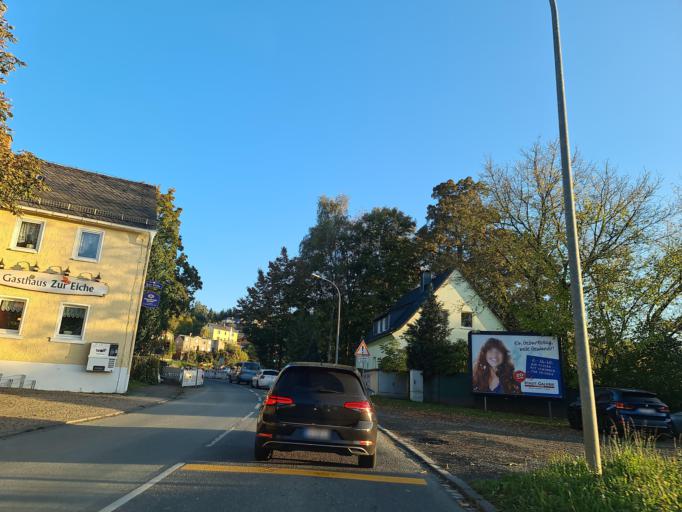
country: DE
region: Saxony
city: Elsterberg
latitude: 50.6290
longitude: 12.1843
